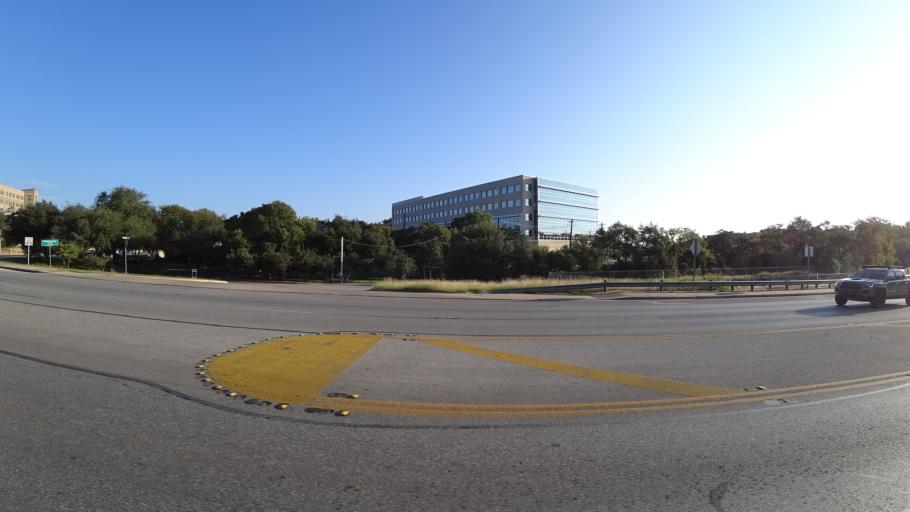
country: US
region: Texas
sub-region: Travis County
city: Rollingwood
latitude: 30.2671
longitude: -97.7854
